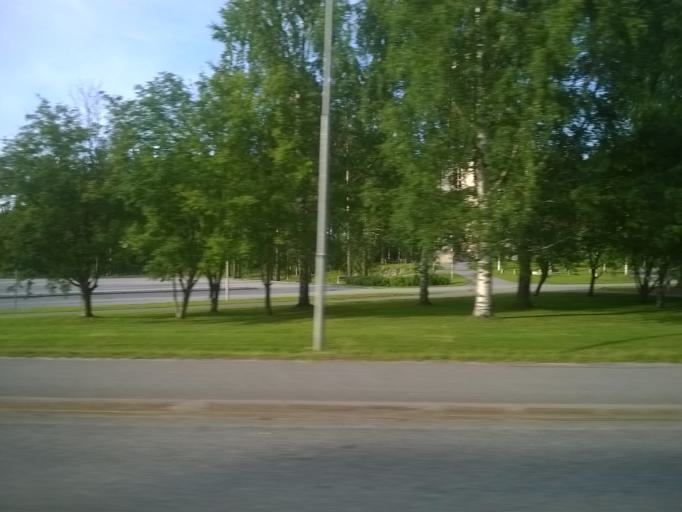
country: FI
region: Kainuu
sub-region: Kajaani
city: Sotkamo
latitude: 64.1309
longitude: 28.4040
